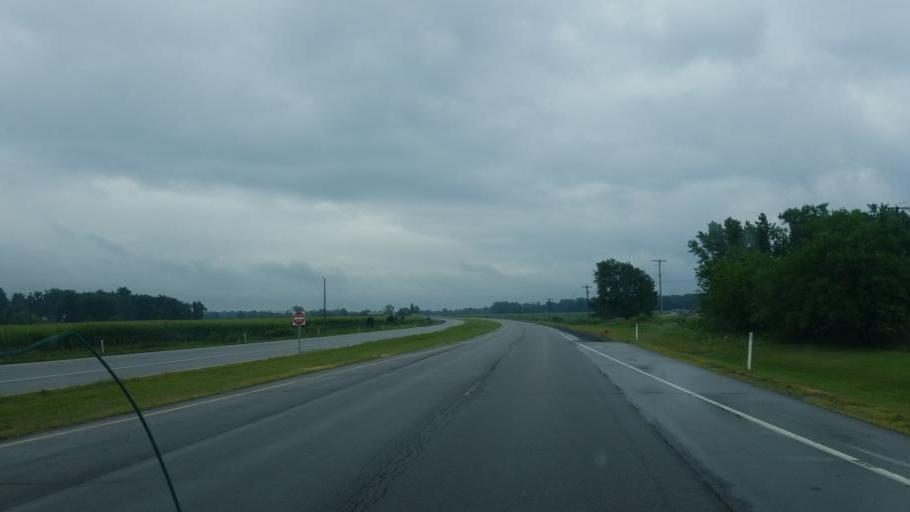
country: US
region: Indiana
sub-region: Wells County
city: Ossian
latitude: 40.9613
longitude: -85.0740
